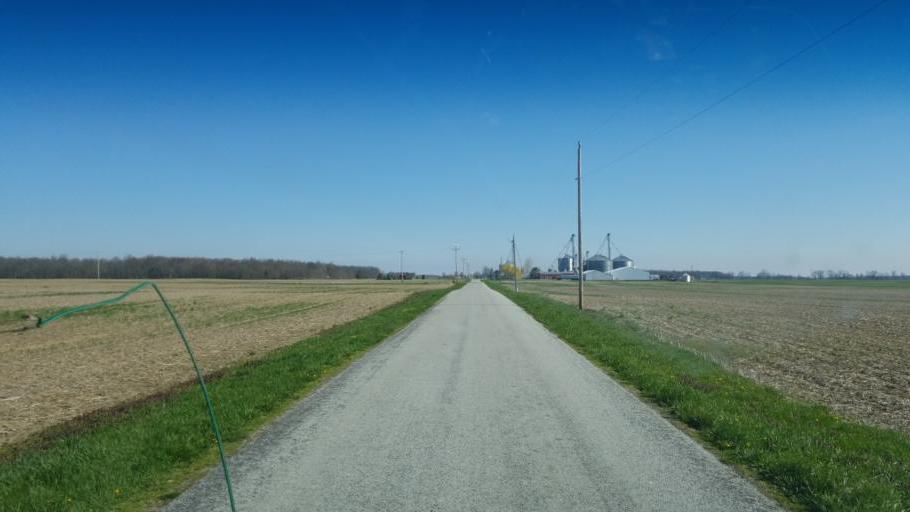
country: US
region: Ohio
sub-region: Hardin County
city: Kenton
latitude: 40.6714
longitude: -83.5620
